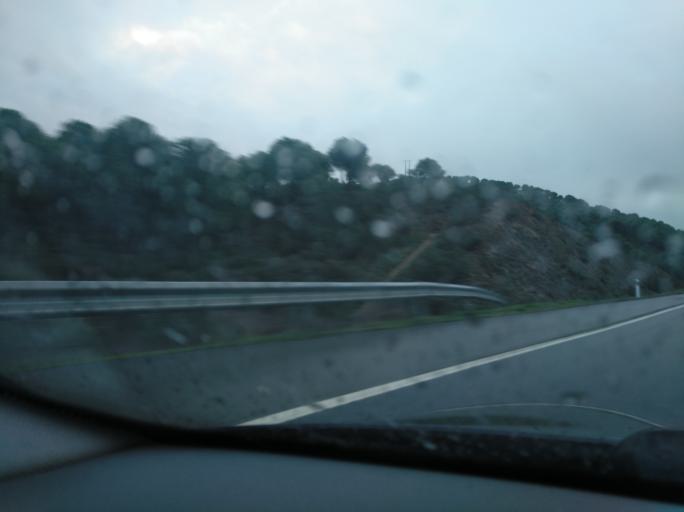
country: PT
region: Faro
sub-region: Alcoutim
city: Alcoutim
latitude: 37.3466
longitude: -7.5078
